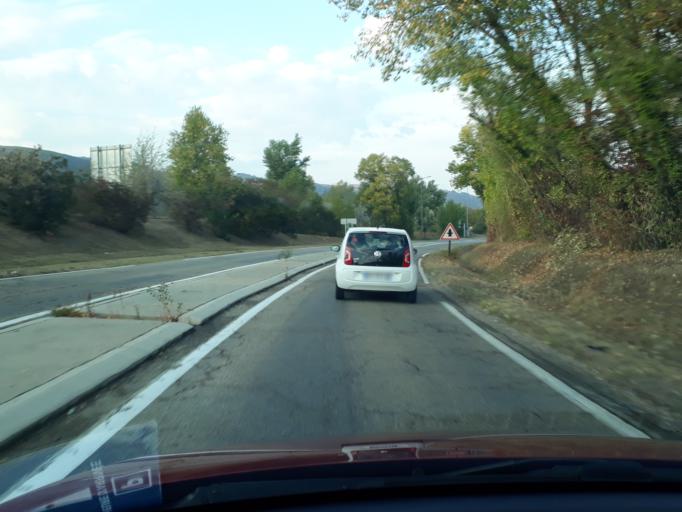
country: FR
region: Rhone-Alpes
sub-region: Departement du Rhone
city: Ampuis
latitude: 45.4892
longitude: 4.8239
